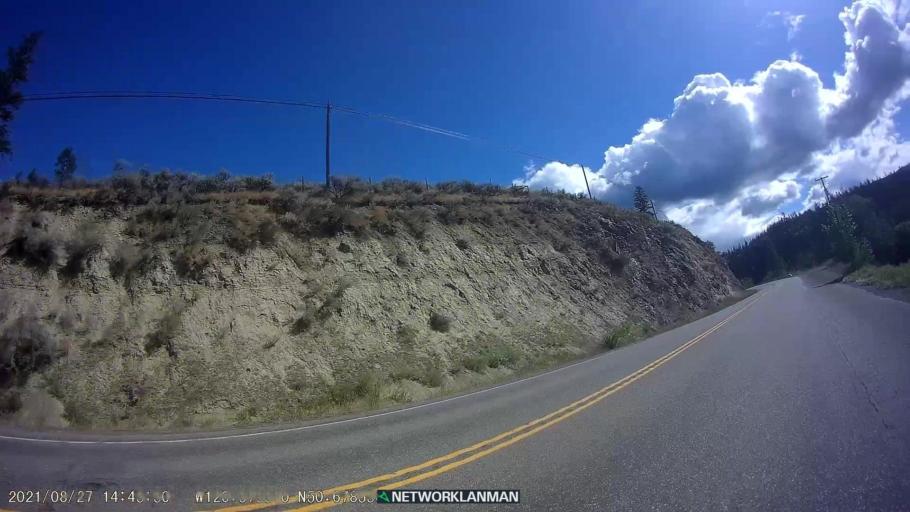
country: CA
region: British Columbia
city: Kamloops
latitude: 50.6783
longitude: -120.5755
